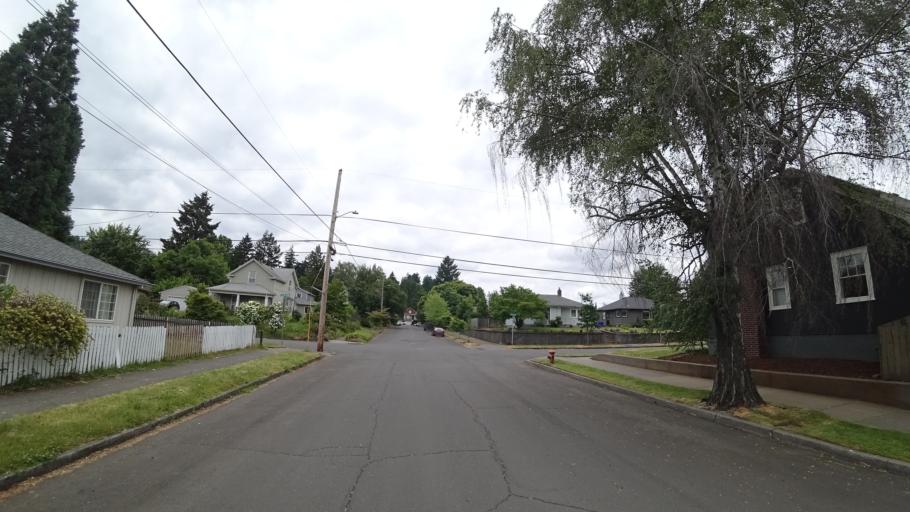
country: US
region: Oregon
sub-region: Multnomah County
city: Lents
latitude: 45.5203
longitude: -122.5844
